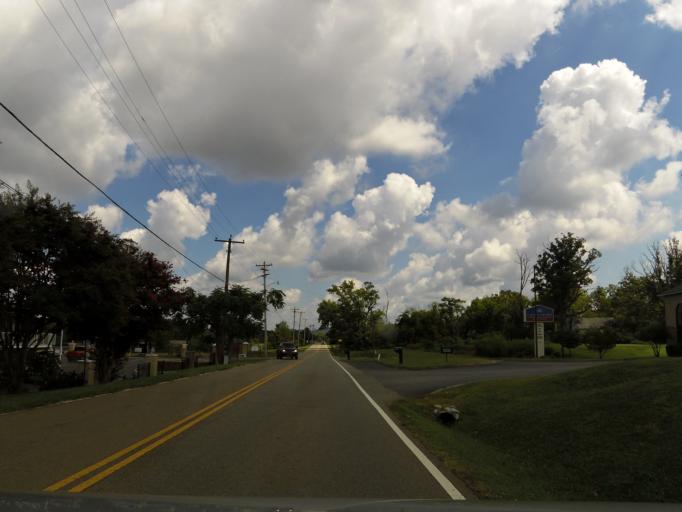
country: US
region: Tennessee
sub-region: Blount County
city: Alcoa
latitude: 35.8125
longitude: -83.9820
